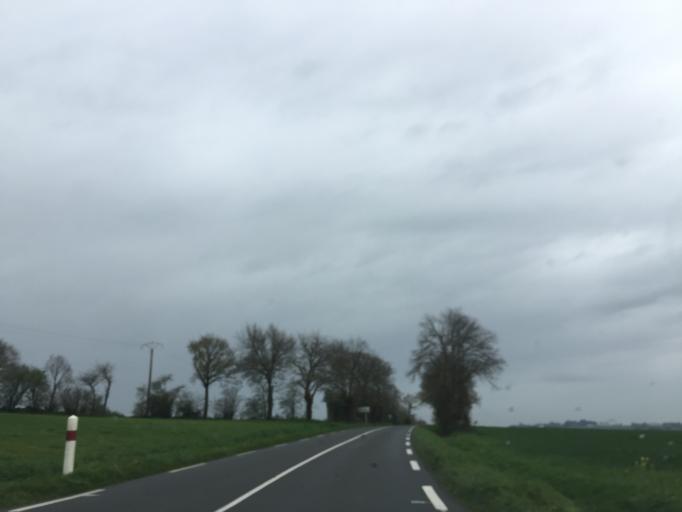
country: FR
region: Pays de la Loire
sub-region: Departement de la Loire-Atlantique
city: Moisdon-la-Riviere
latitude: 47.6197
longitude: -1.3785
